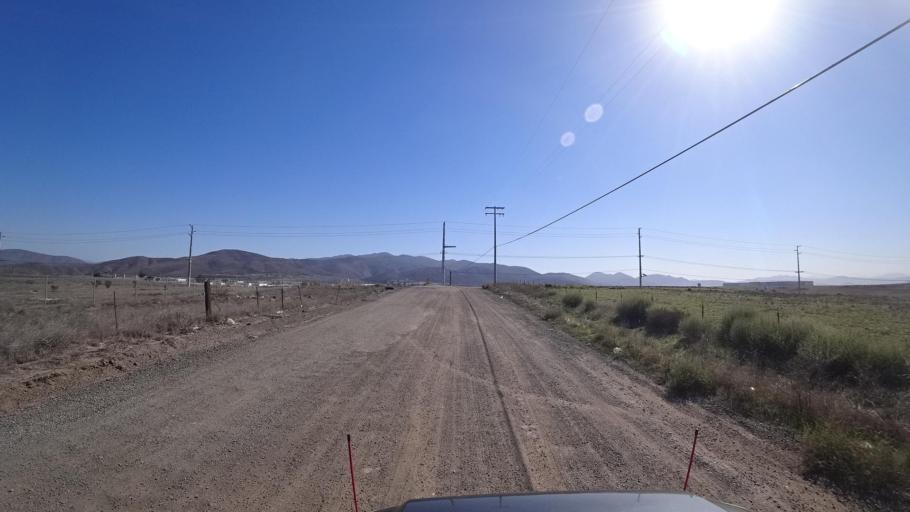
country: MX
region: Baja California
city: Tijuana
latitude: 32.5785
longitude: -116.9462
